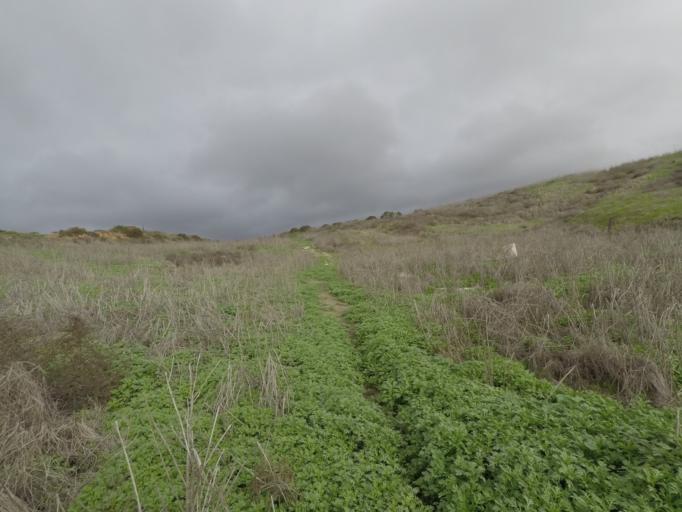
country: MX
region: Baja California
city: Tijuana
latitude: 32.5542
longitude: -117.0376
